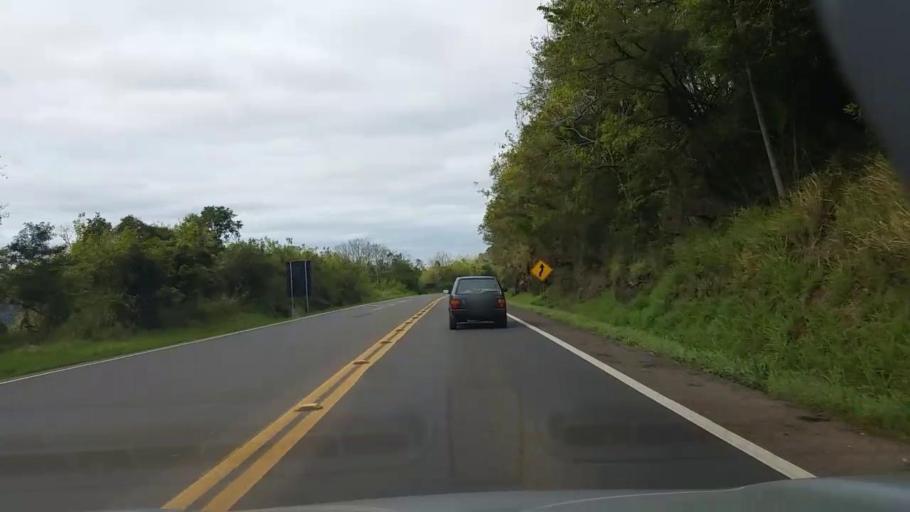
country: BR
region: Rio Grande do Sul
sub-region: Arroio Do Meio
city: Arroio do Meio
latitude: -29.3859
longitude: -52.0519
